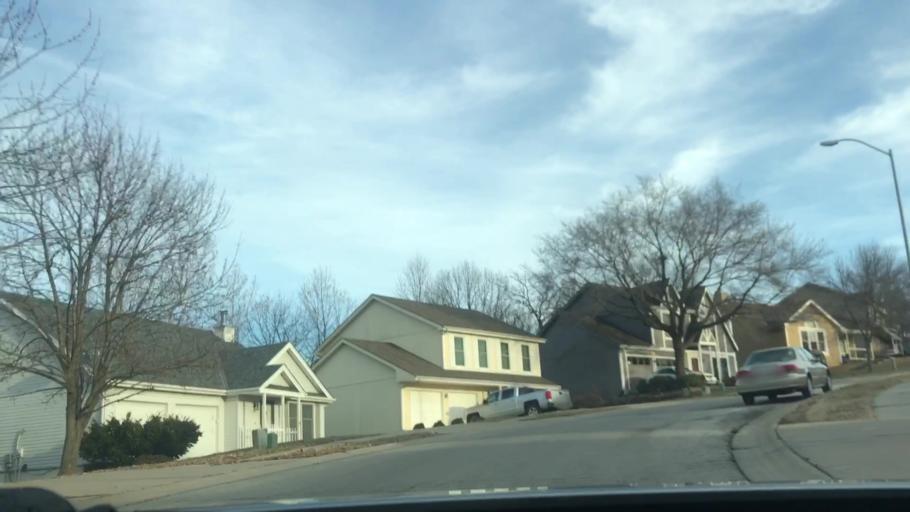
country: US
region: Missouri
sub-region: Platte County
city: Riverside
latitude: 39.2087
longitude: -94.5938
